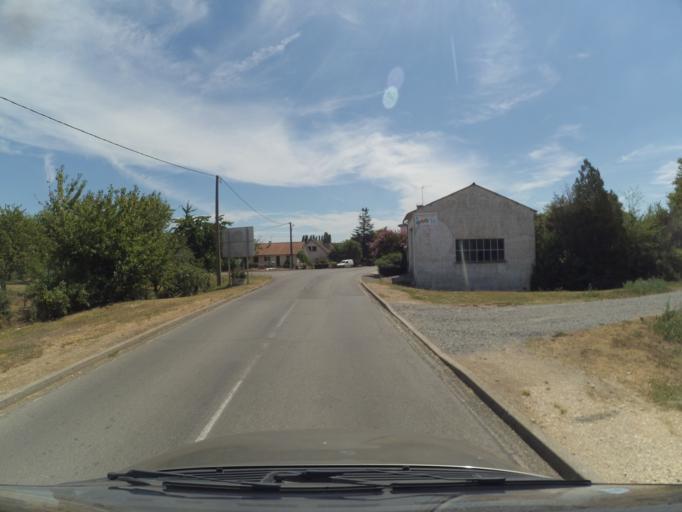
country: FR
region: Poitou-Charentes
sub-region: Departement de la Vienne
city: Usson-du-Poitou
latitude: 46.2208
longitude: 0.5305
